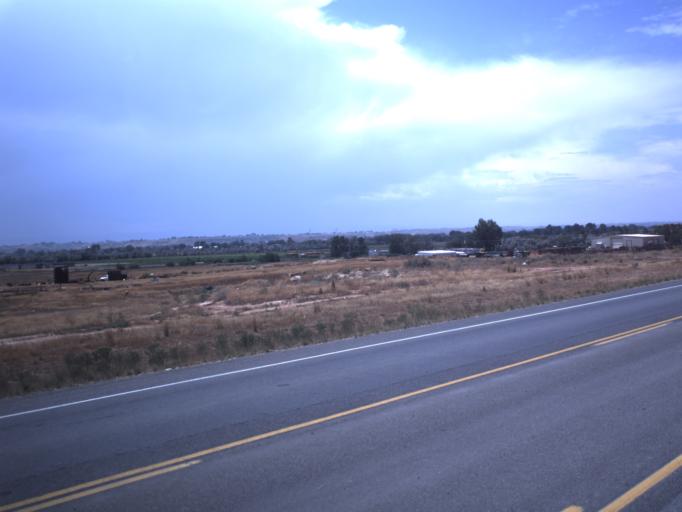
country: US
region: Utah
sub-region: Duchesne County
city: Roosevelt
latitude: 40.3023
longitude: -109.9486
